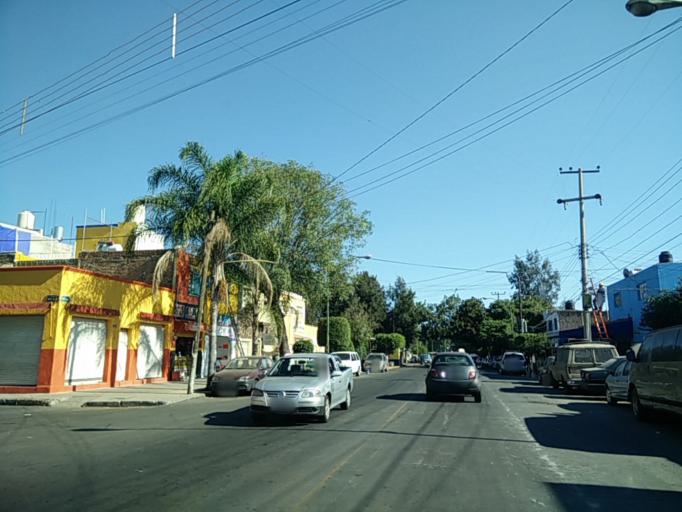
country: MX
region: Jalisco
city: Tlaquepaque
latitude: 20.6566
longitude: -103.3307
